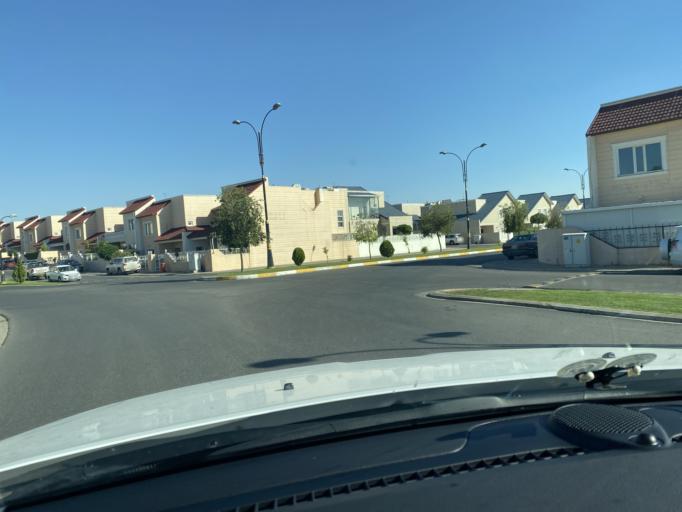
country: IQ
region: Arbil
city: Erbil
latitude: 36.2413
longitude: 44.0506
